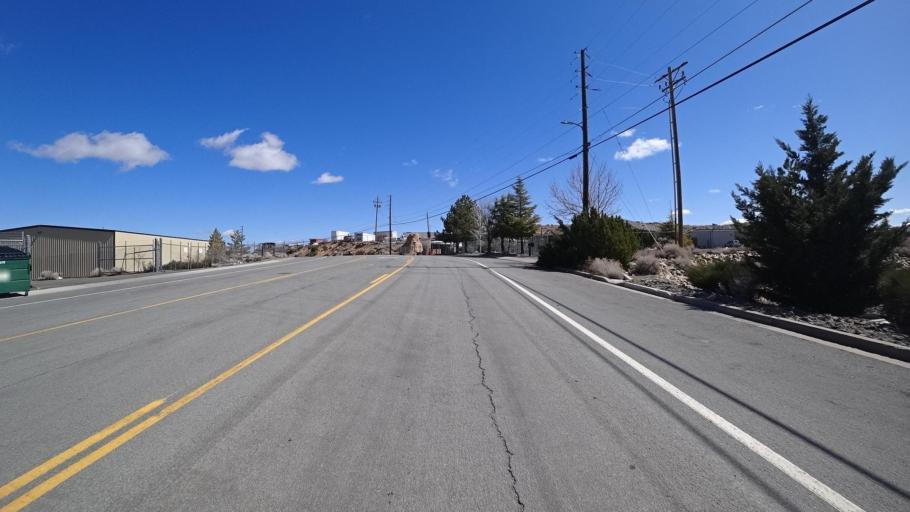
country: US
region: Nevada
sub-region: Washoe County
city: Golden Valley
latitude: 39.5923
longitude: -119.8339
